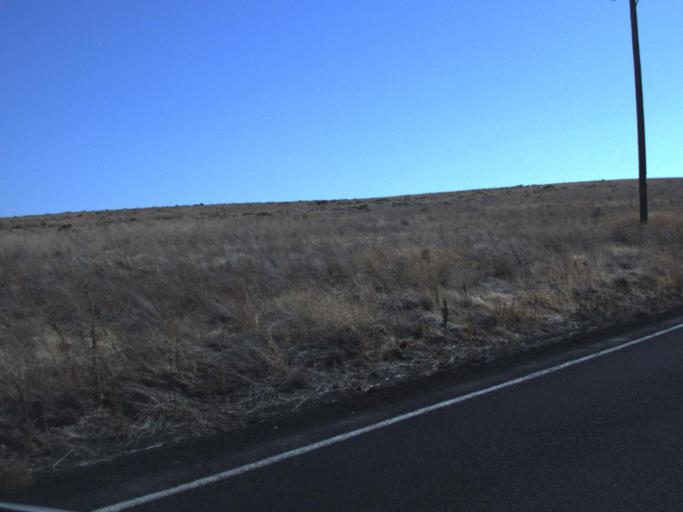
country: US
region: Washington
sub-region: Adams County
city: Ritzville
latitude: 47.0790
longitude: -118.6629
